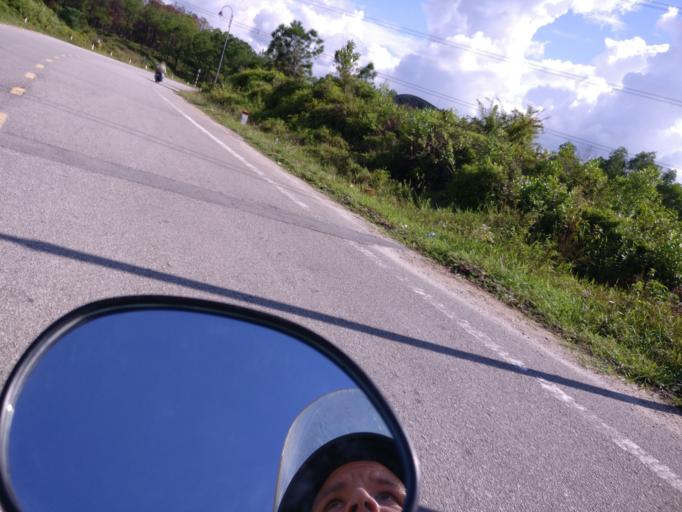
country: VN
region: Thua Thien-Hue
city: Hue
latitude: 16.4062
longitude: 107.5897
